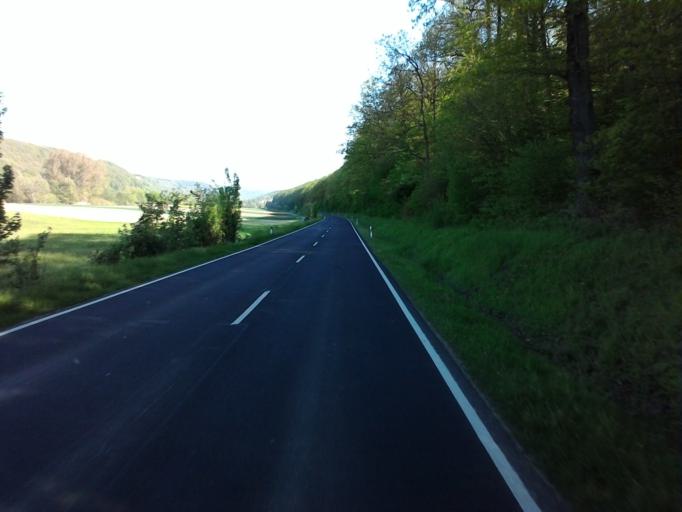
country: DE
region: Bavaria
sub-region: Regierungsbezirk Unterfranken
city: Hafenlohr
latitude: 49.8746
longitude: 9.6066
